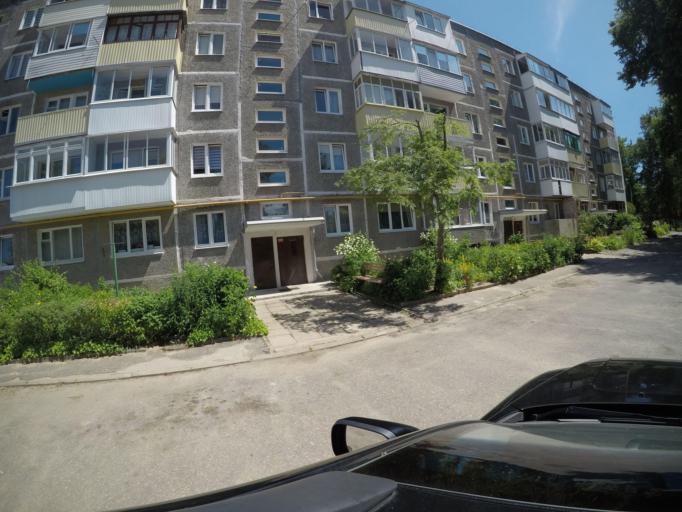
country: BY
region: Grodnenskaya
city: Hrodna
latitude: 53.6971
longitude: 23.8122
